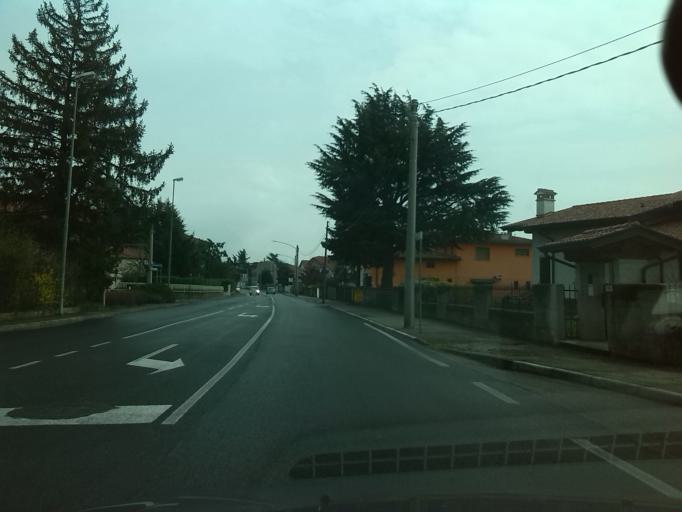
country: IT
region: Friuli Venezia Giulia
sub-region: Provincia di Gorizia
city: Mossa
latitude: 45.9353
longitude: 13.5652
